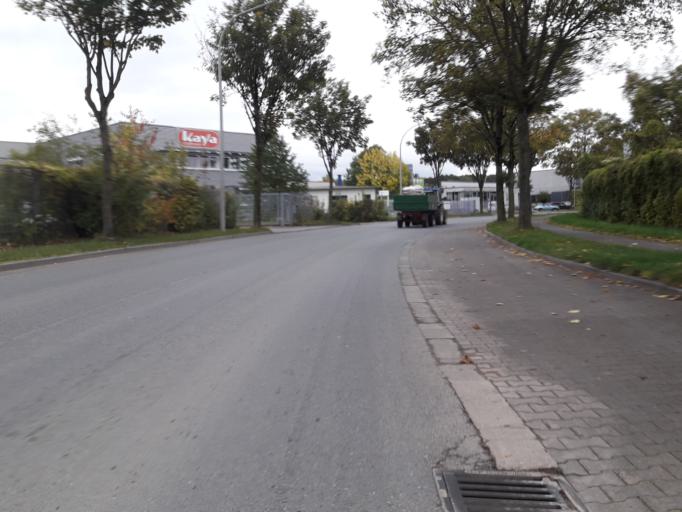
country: DE
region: North Rhine-Westphalia
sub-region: Regierungsbezirk Detmold
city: Paderborn
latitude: 51.6919
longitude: 8.7466
